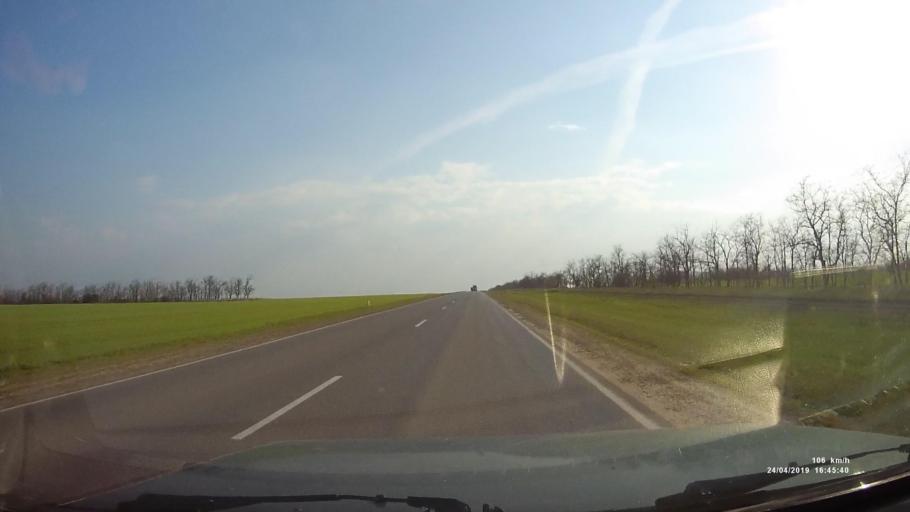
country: RU
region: Rostov
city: Gundorovskiy
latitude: 46.7667
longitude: 41.8117
